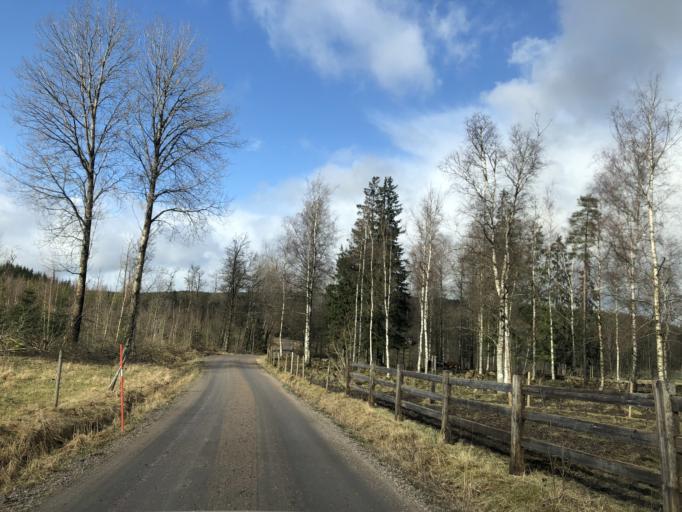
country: SE
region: Vaestra Goetaland
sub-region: Boras Kommun
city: Dalsjofors
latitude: 57.8251
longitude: 13.2061
